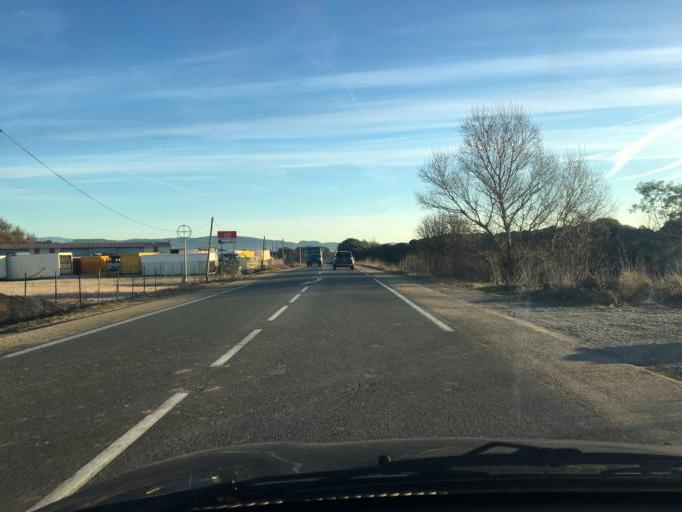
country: FR
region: Provence-Alpes-Cote d'Azur
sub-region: Departement du Var
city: Les Arcs
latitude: 43.4563
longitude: 6.5156
